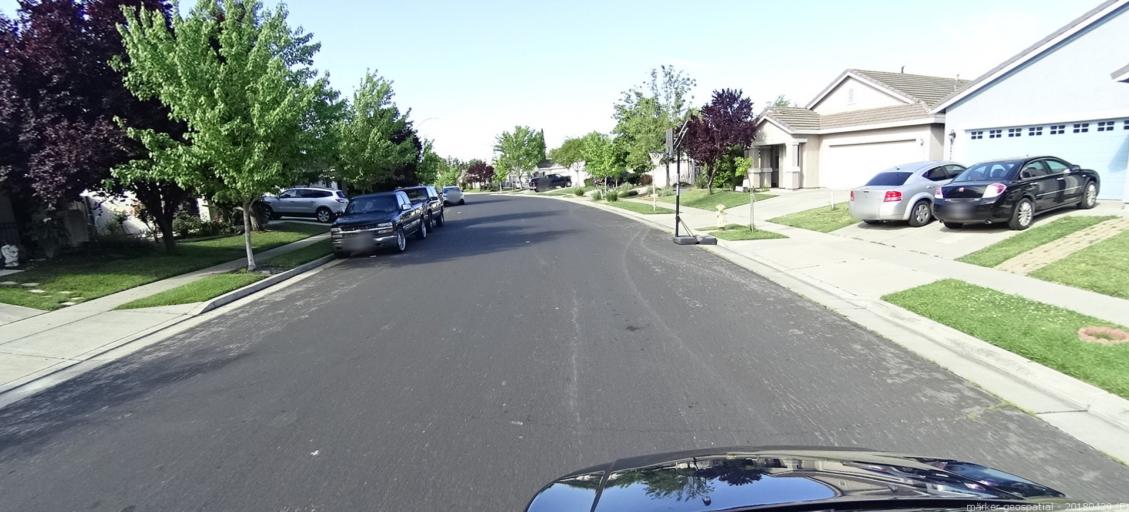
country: US
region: California
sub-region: Yolo County
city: West Sacramento
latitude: 38.5395
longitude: -121.5695
